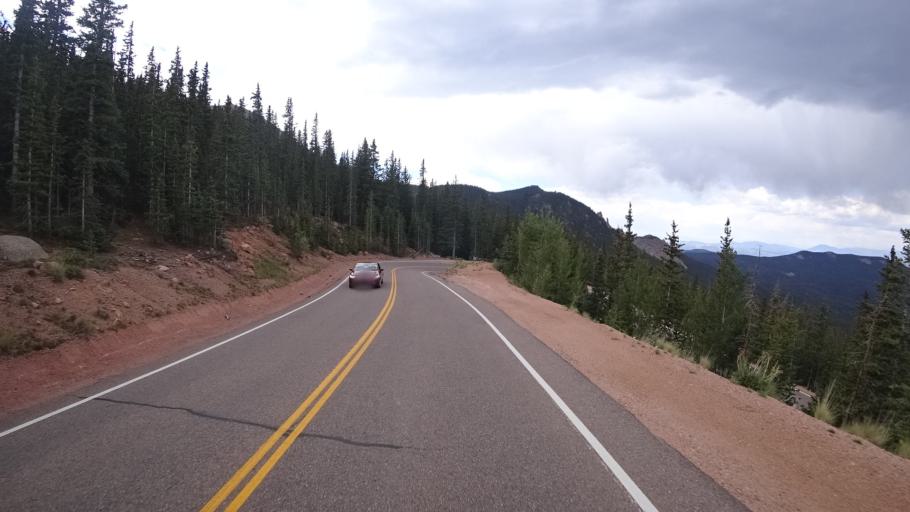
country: US
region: Colorado
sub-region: El Paso County
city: Cascade-Chipita Park
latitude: 38.8873
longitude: -105.0726
